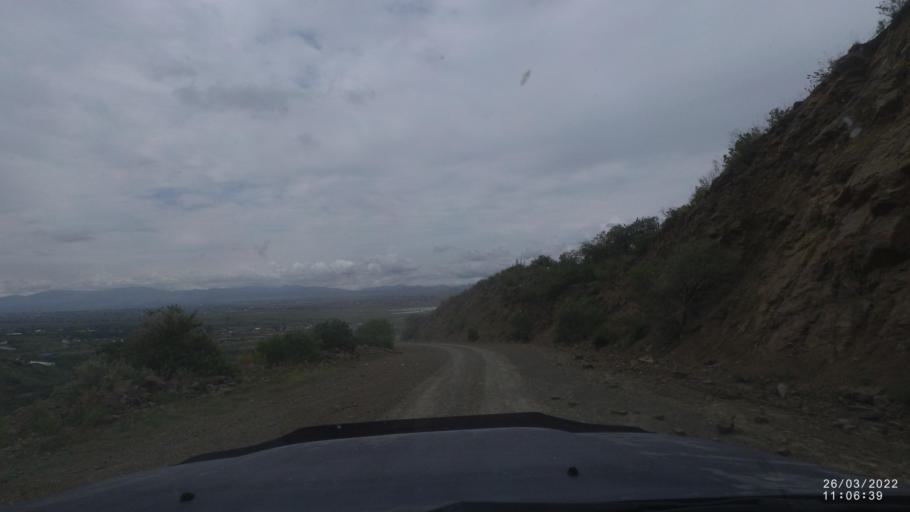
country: BO
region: Cochabamba
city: Tarata
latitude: -17.5341
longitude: -66.0173
